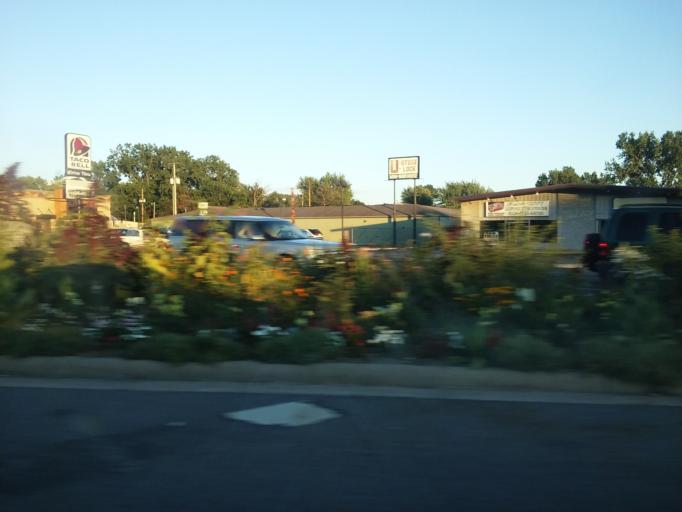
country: US
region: Ohio
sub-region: Hancock County
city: Findlay
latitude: 41.0492
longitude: -83.6301
